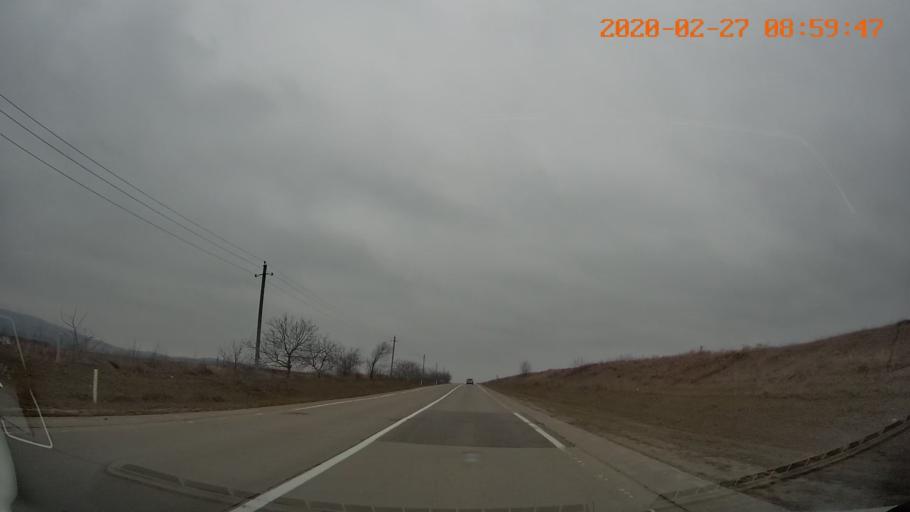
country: MD
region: Singerei
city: Bilicenii Vechi
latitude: 47.5136
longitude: 28.0616
